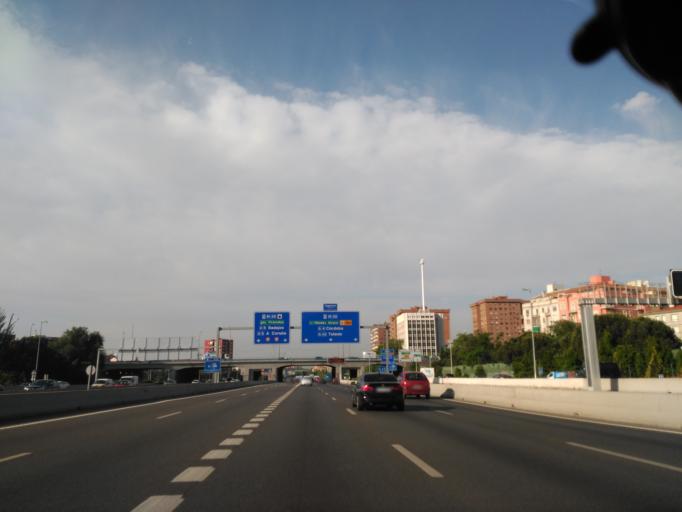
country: ES
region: Madrid
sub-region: Provincia de Madrid
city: Puente de Vallecas
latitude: 40.4081
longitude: -3.6645
